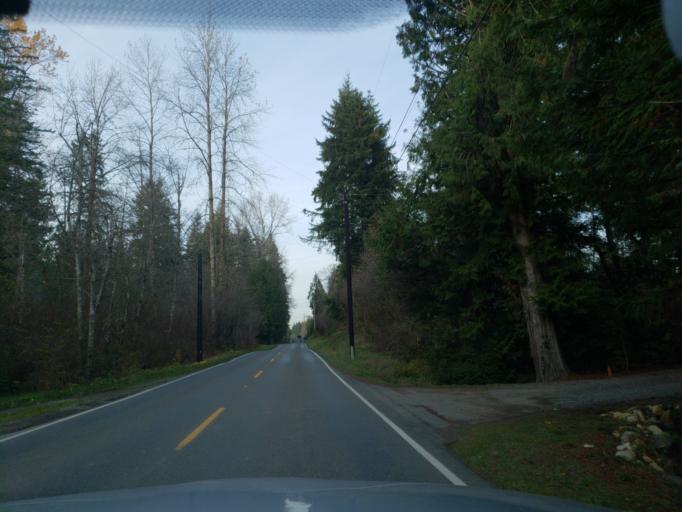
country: US
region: Washington
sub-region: Snohomish County
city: Cathcart
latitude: 47.8216
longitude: -122.0769
